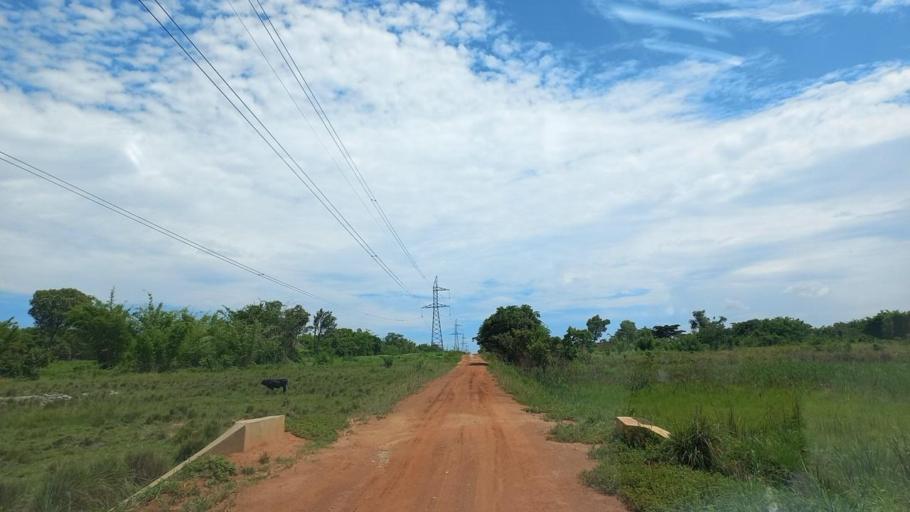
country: ZM
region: Copperbelt
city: Kitwe
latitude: -12.8083
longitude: 28.3611
